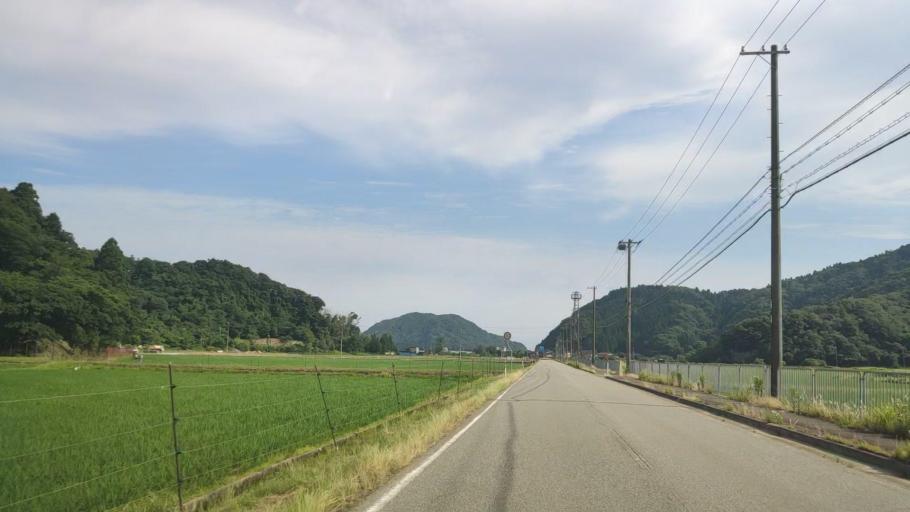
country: JP
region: Hyogo
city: Toyooka
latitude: 35.6285
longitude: 134.8410
